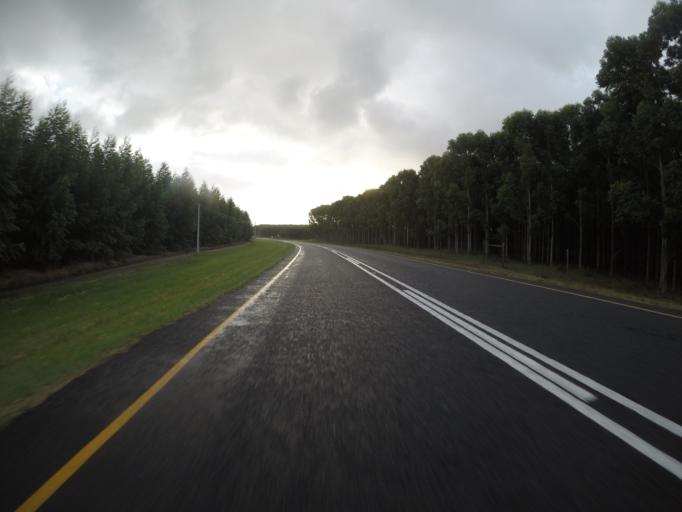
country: ZA
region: KwaZulu-Natal
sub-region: uMkhanyakude District Municipality
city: Mtubatuba
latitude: -28.3670
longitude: 32.2623
